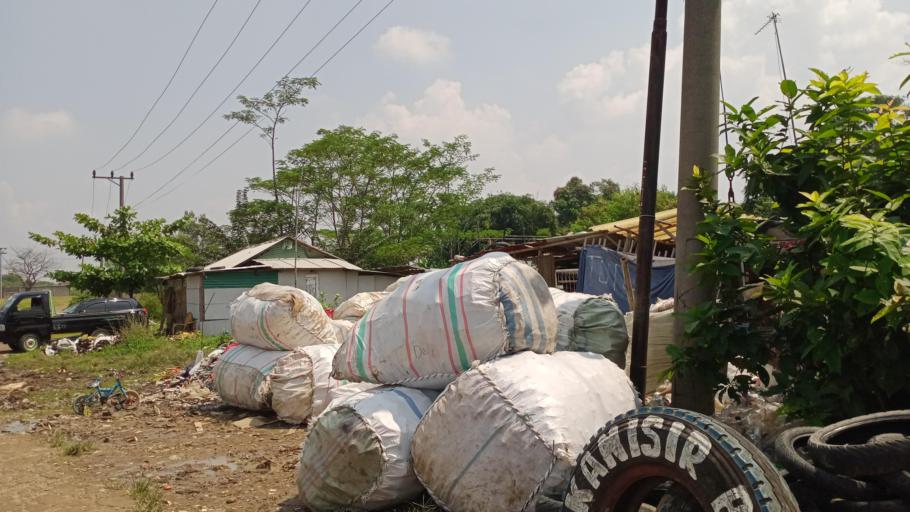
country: ID
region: West Java
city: Cileungsir
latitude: -6.4070
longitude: 107.1010
